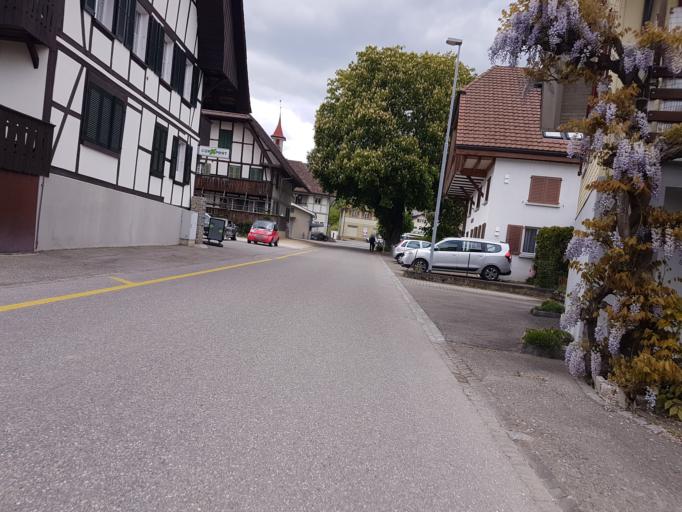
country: CH
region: Bern
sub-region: Biel/Bienne District
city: Orpund
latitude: 47.1491
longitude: 7.3240
